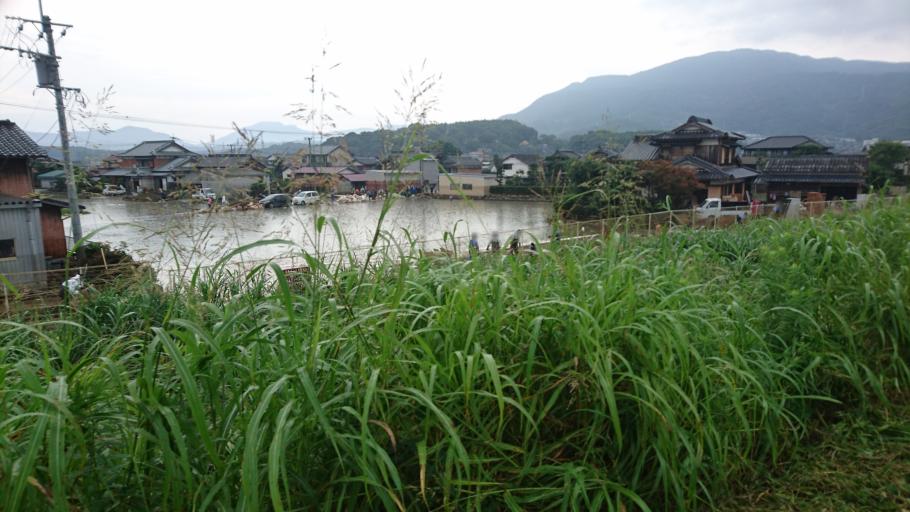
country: JP
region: Saga Prefecture
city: Takeocho-takeo
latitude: 33.2089
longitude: 130.1058
